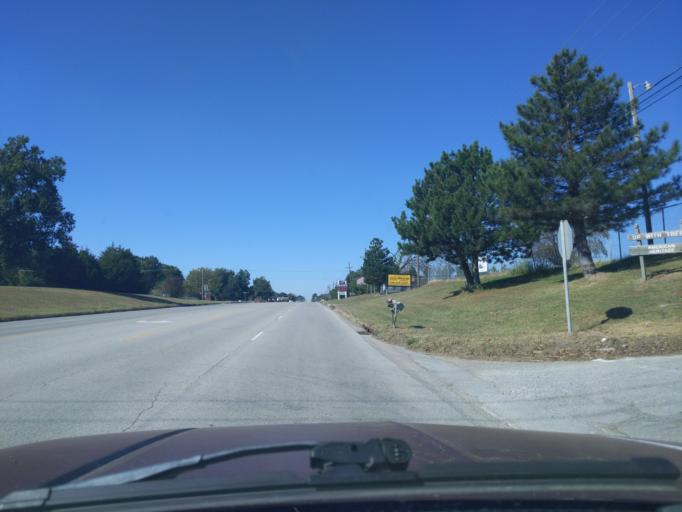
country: US
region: Oklahoma
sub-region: Creek County
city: Kiefer
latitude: 35.9885
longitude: -96.0681
